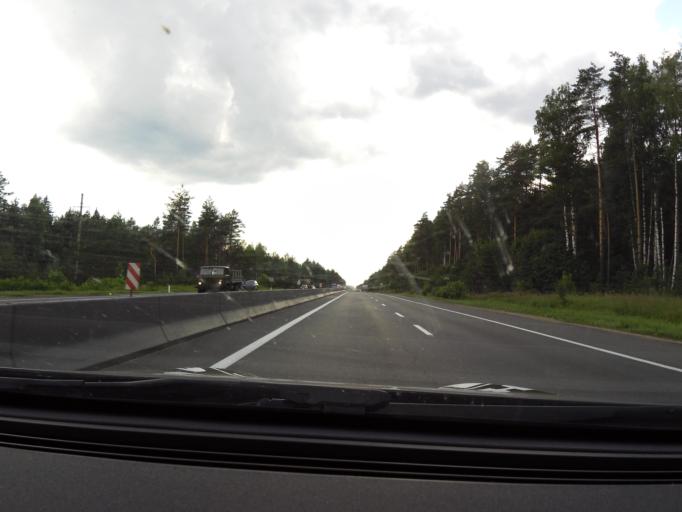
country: RU
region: Nizjnij Novgorod
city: Yuganets
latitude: 56.2873
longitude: 43.2149
